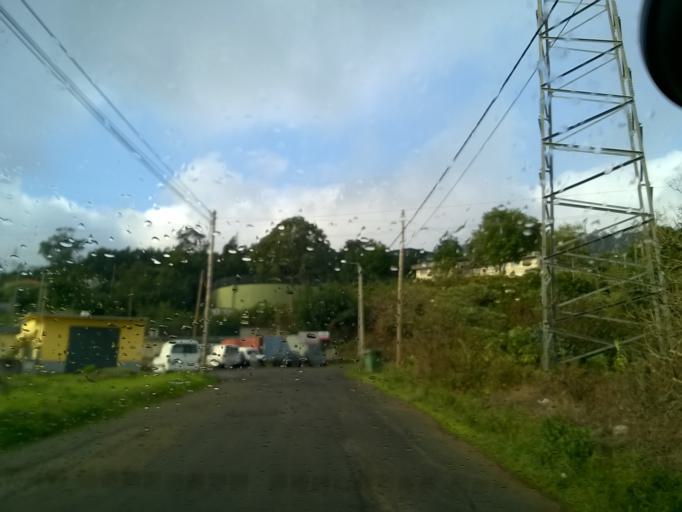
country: PT
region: Madeira
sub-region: Santa Cruz
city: Camacha
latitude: 32.6636
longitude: -16.8658
